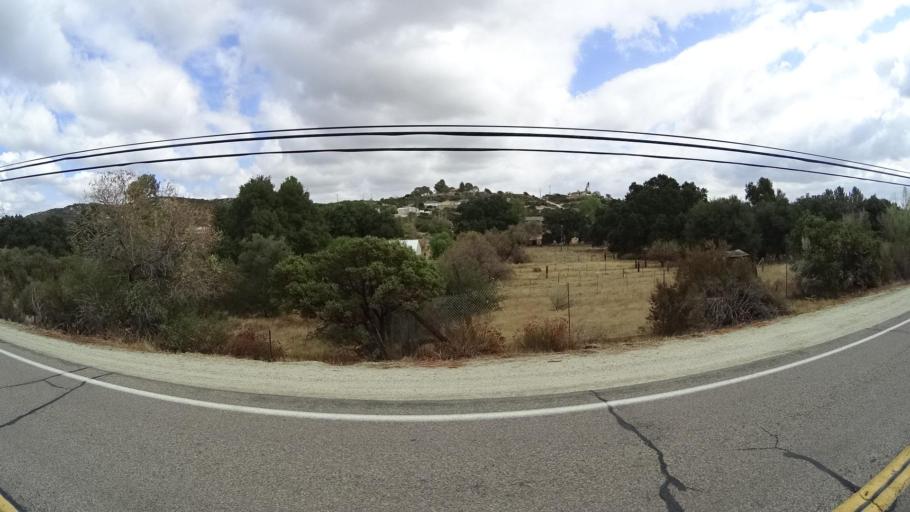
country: US
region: California
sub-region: San Diego County
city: Campo
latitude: 32.6472
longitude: -116.4873
